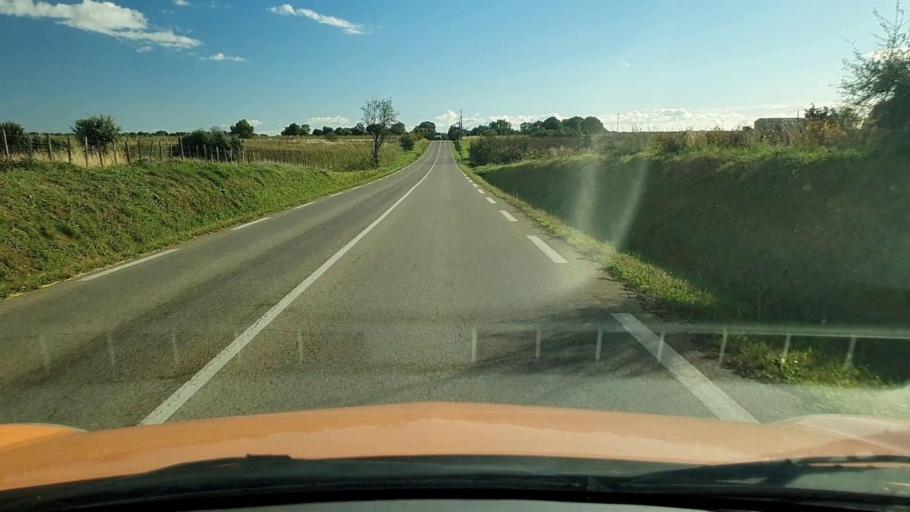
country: FR
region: Languedoc-Roussillon
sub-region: Departement du Gard
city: Vauvert
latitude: 43.6743
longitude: 4.2806
